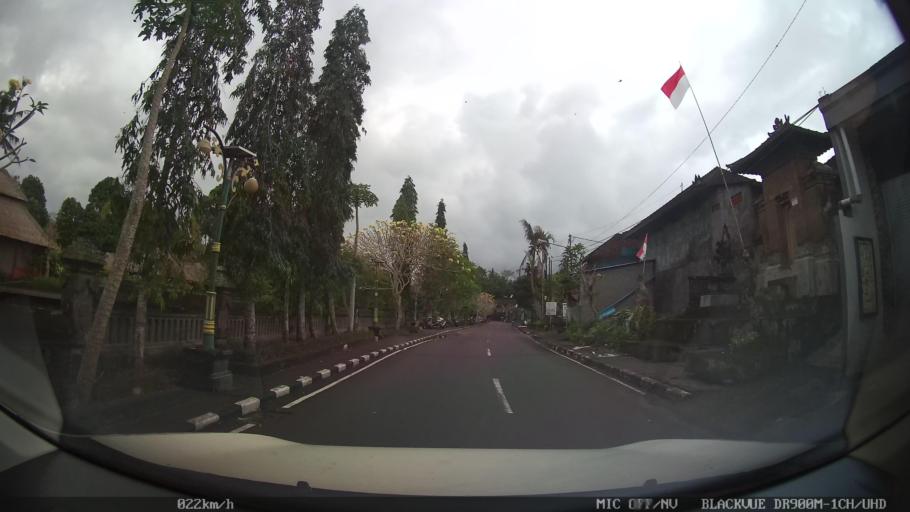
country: ID
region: Bali
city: Banjar Serangan
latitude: -8.5433
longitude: 115.1733
